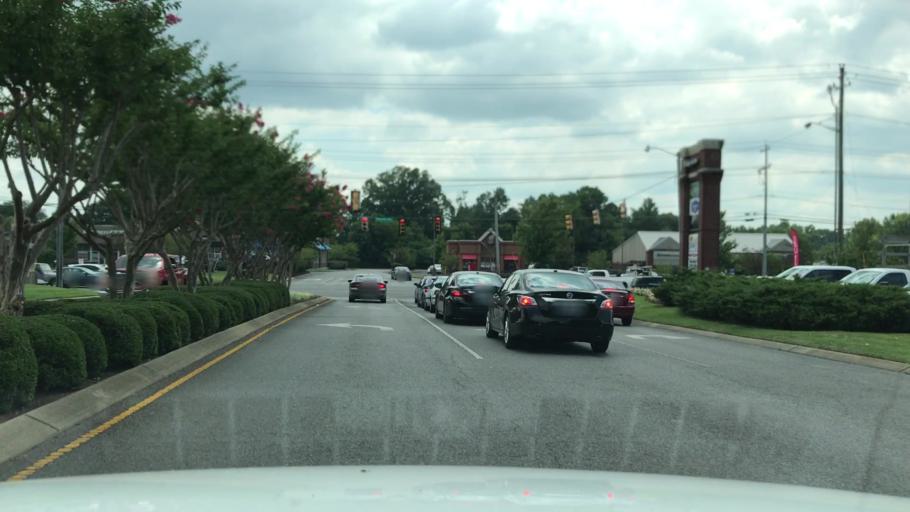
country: US
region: Tennessee
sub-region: Sumner County
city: Gallatin
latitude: 36.3769
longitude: -86.4727
